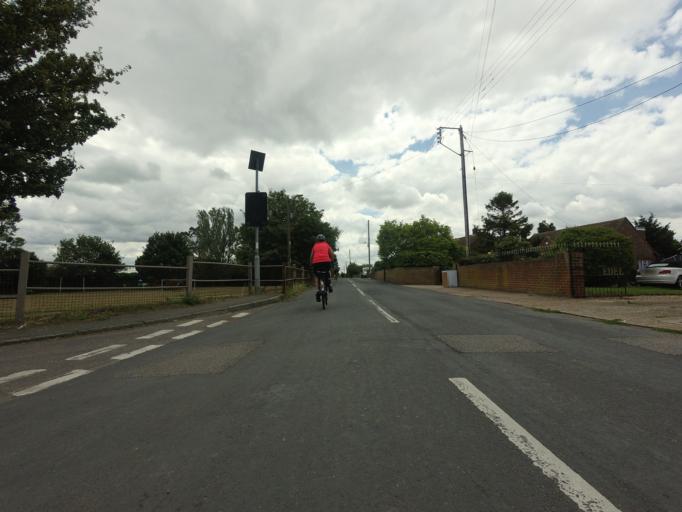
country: GB
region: England
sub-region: Medway
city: Allhallows
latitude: 51.4557
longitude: 0.6360
